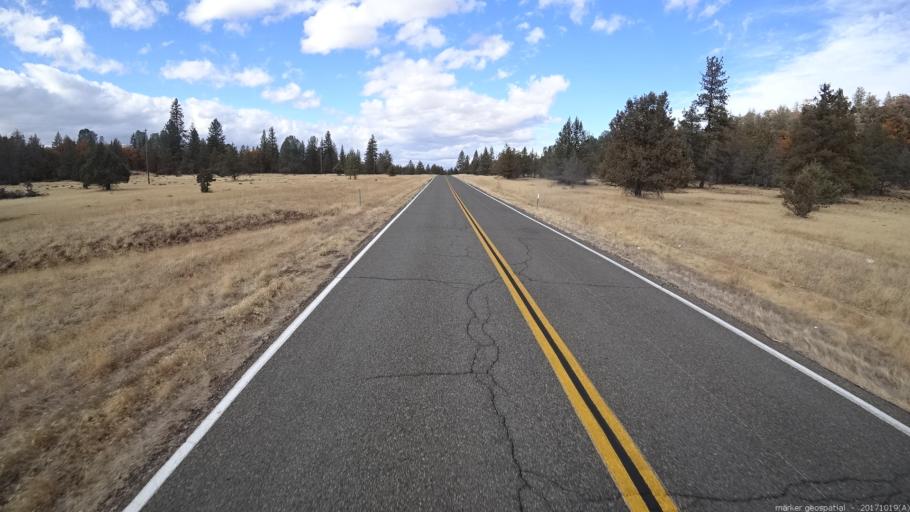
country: US
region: California
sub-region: Shasta County
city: Burney
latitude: 40.9808
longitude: -121.4333
